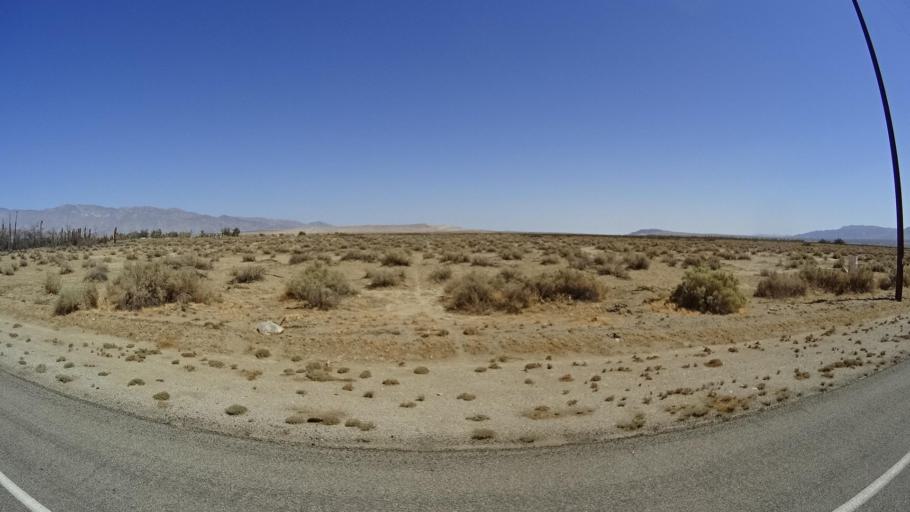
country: US
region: California
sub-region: San Diego County
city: Borrego Springs
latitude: 33.2514
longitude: -116.3478
